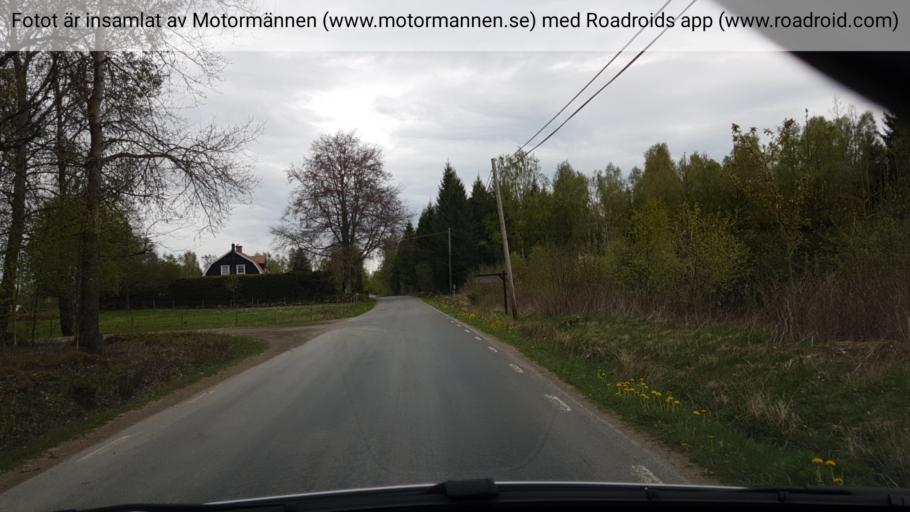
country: SE
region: Vaestra Goetaland
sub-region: Skara Kommun
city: Skara
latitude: 58.3571
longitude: 13.4984
